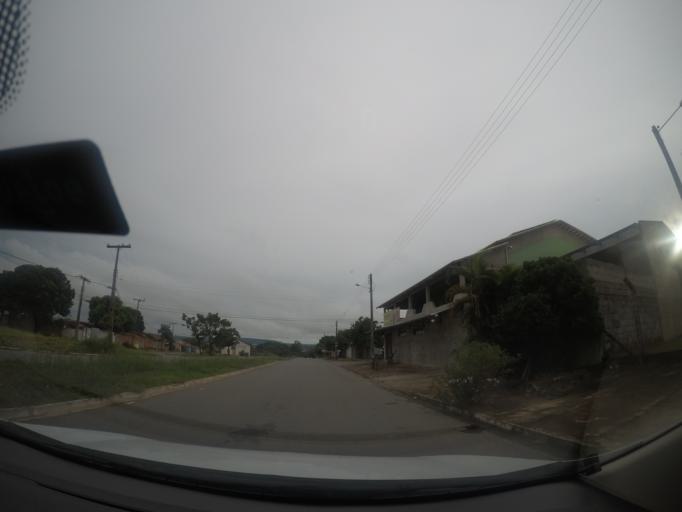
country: BR
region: Goias
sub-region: Goiania
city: Goiania
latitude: -16.7517
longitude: -49.3115
